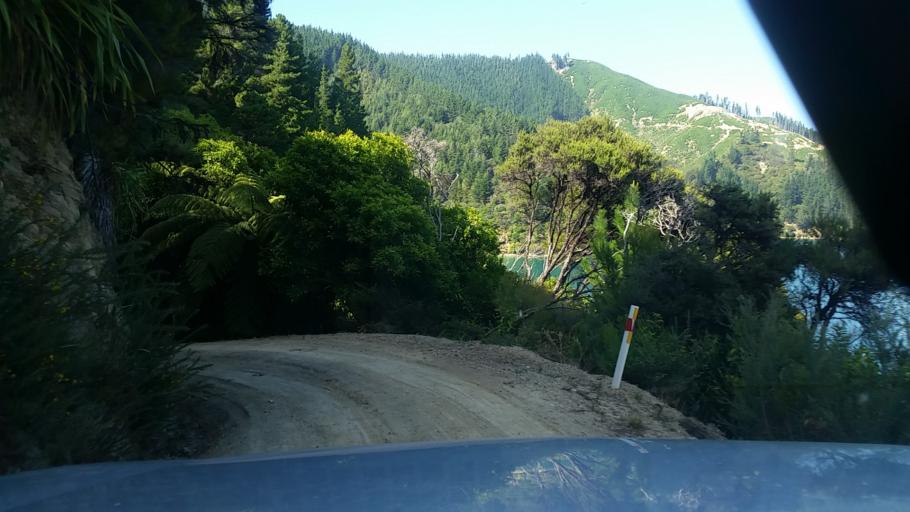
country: NZ
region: Marlborough
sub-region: Marlborough District
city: Picton
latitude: -41.3100
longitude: 174.1711
